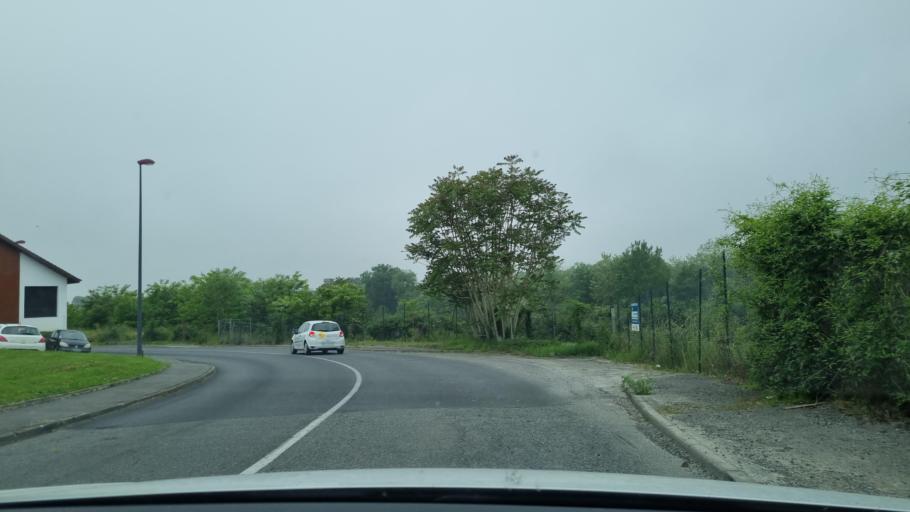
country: FR
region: Aquitaine
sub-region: Departement des Pyrenees-Atlantiques
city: Orthez
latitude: 43.4822
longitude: -0.7669
